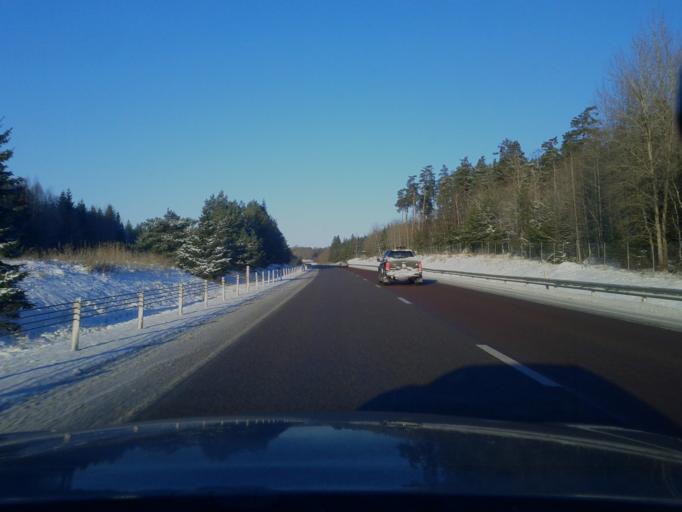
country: SE
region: Uppsala
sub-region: Uppsala Kommun
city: Alsike
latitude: 59.7719
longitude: 17.7869
